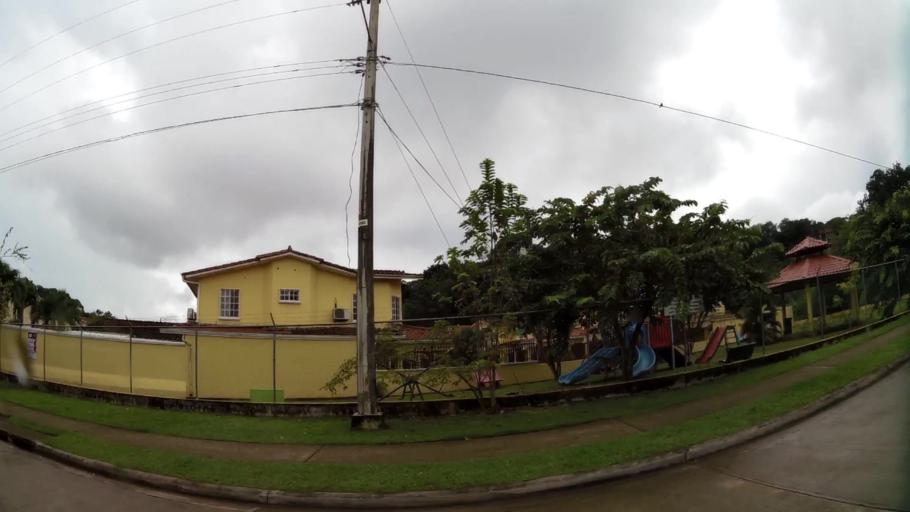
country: PA
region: Panama
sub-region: Distrito de Panama
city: Ancon
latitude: 8.9897
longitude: -79.5613
